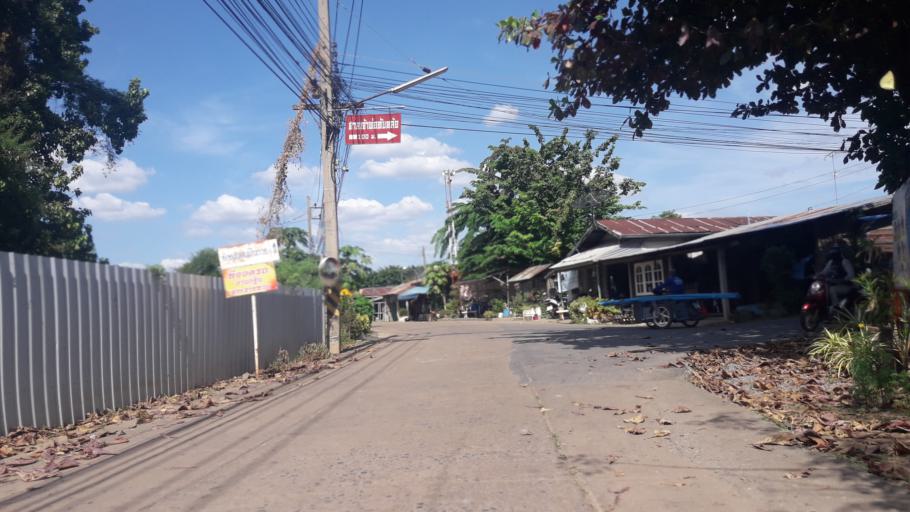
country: TH
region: Phichit
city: Thap Khlo
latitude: 16.1696
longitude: 100.5767
